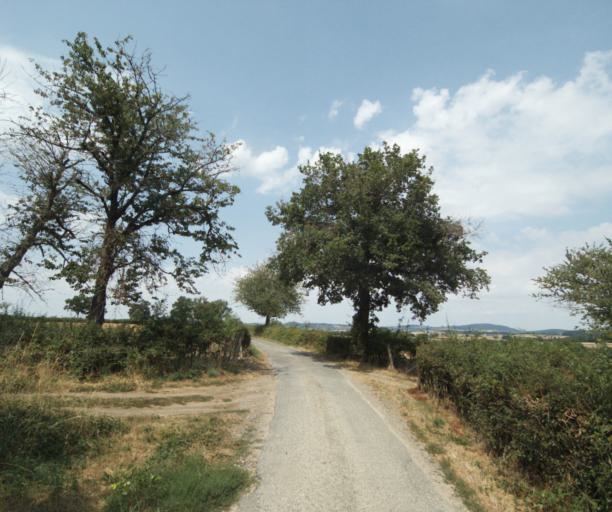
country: FR
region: Bourgogne
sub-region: Departement de Saone-et-Loire
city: Gueugnon
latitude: 46.6064
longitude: 4.0166
